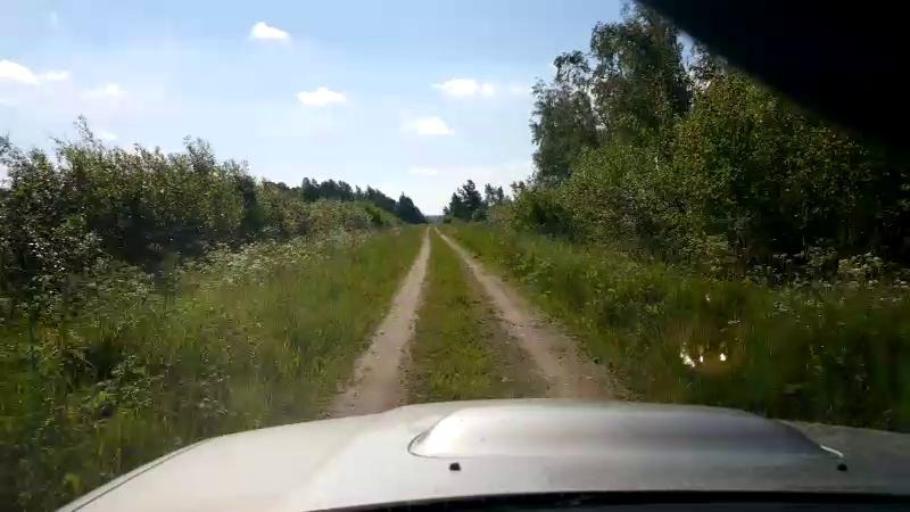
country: EE
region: Paernumaa
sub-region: Sindi linn
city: Sindi
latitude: 58.5030
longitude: 24.6430
